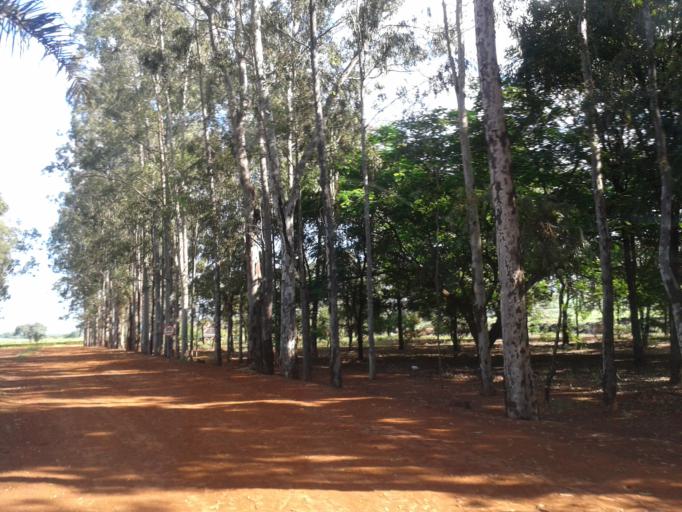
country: BR
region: Minas Gerais
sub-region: Centralina
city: Centralina
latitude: -18.6453
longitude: -49.2420
